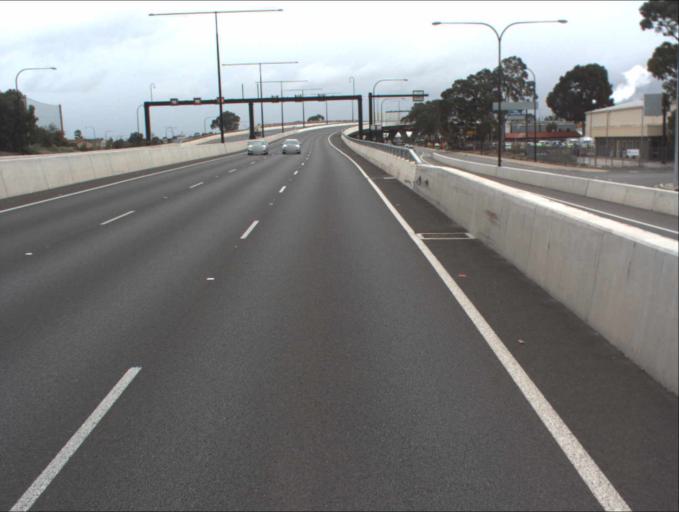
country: AU
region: South Australia
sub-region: Charles Sturt
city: Woodville North
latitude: -34.8615
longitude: 138.5682
